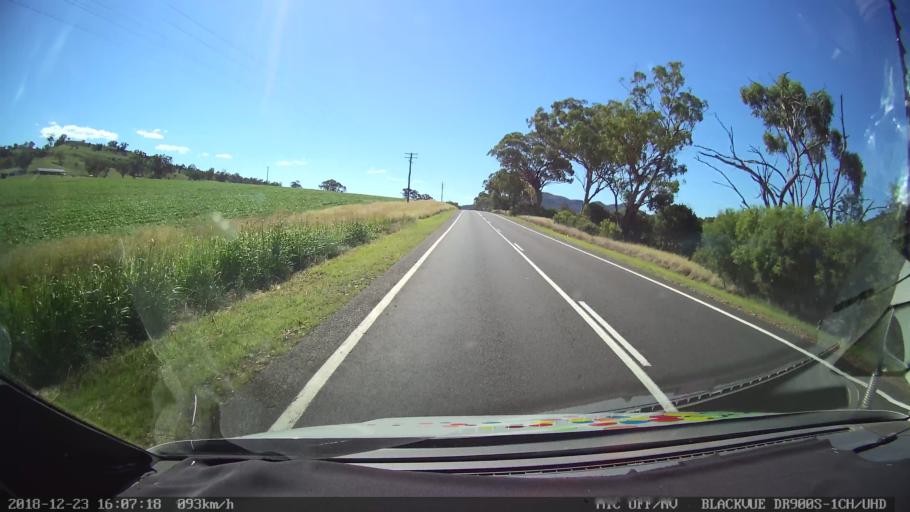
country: AU
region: New South Wales
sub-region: Tamworth Municipality
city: Phillip
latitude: -31.2723
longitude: 150.7640
